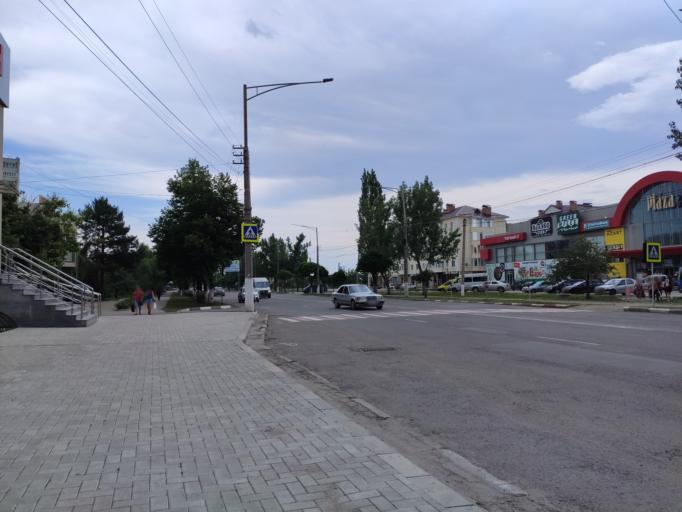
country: MD
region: Balti
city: Balti
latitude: 47.7630
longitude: 27.9410
